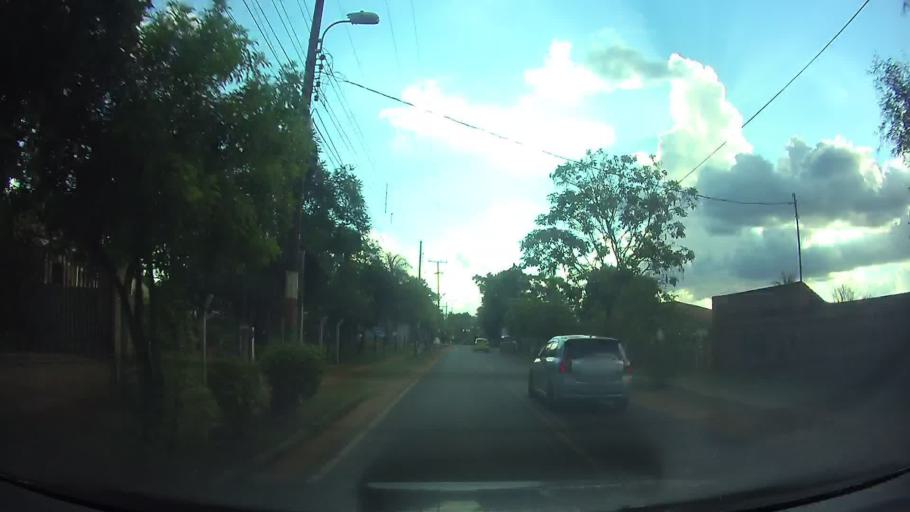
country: PY
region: Central
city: Aregua
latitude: -25.2796
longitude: -57.4327
